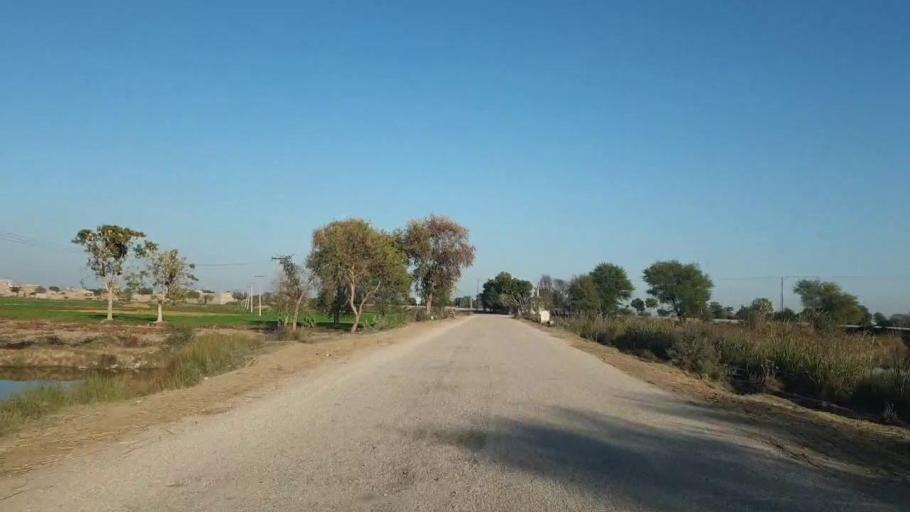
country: PK
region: Sindh
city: Dokri
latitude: 27.3723
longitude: 68.1222
